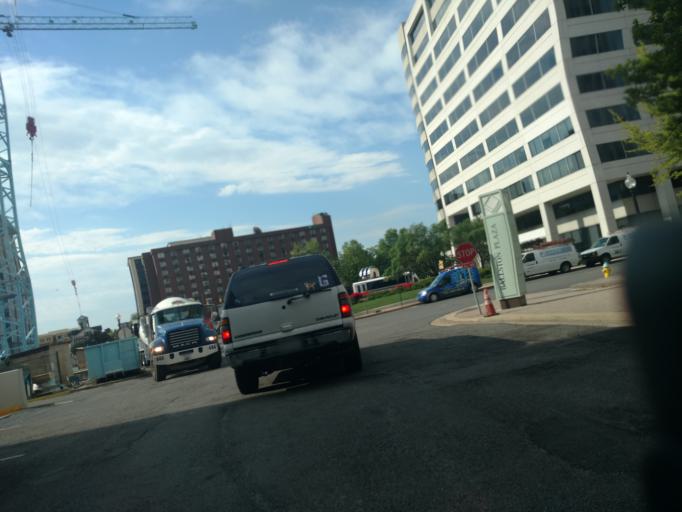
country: US
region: Virginia
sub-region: Arlington County
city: Arlington
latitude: 38.8833
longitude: -77.1175
